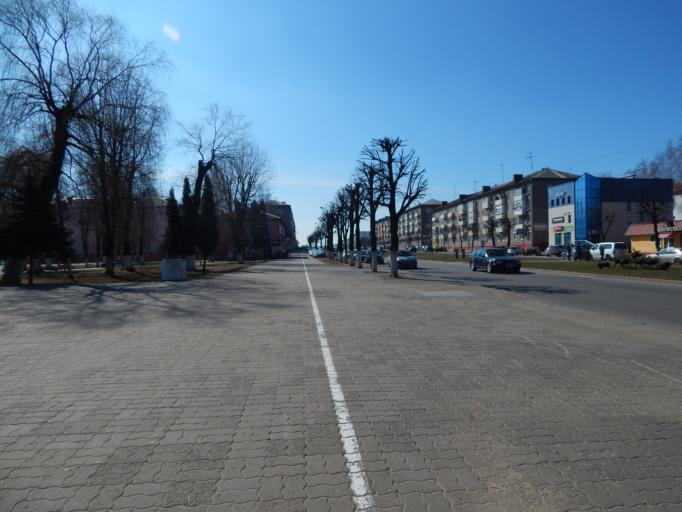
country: BY
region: Minsk
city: Horad Barysaw
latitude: 54.2224
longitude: 28.5111
